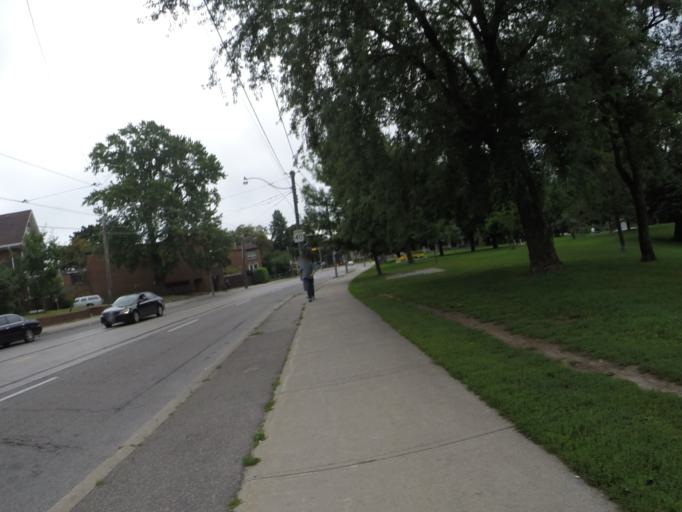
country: CA
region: Ontario
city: Toronto
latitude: 43.6699
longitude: -79.3535
